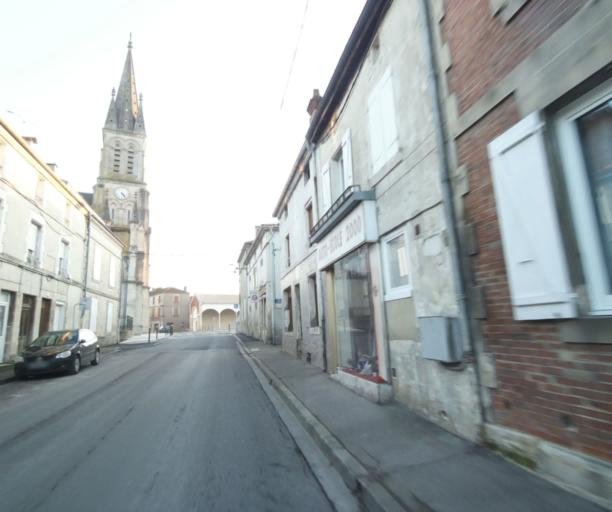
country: FR
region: Champagne-Ardenne
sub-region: Departement de la Haute-Marne
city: Bienville
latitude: 48.5857
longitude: 5.0371
